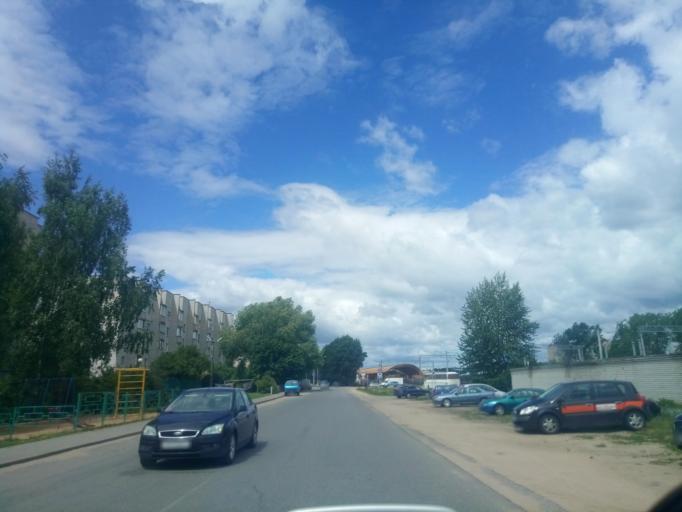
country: BY
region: Minsk
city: Zhdanovichy
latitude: 53.9449
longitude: 27.4299
